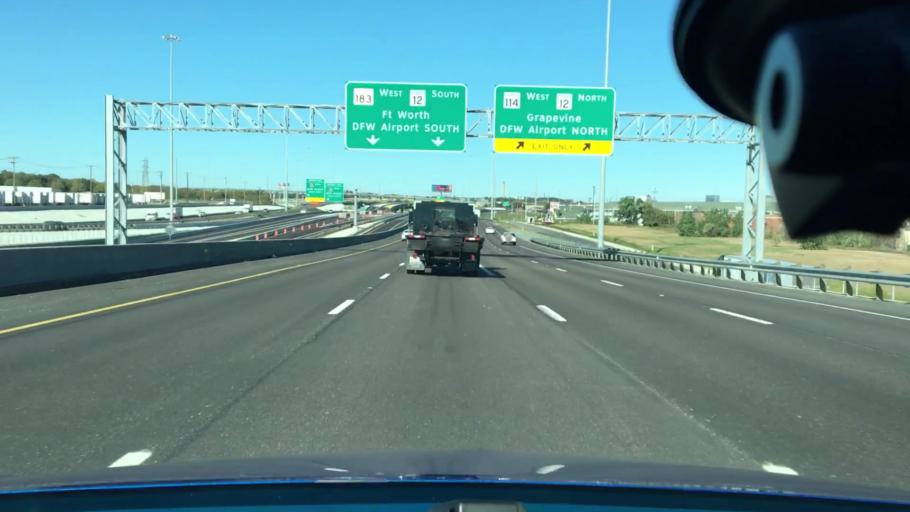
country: US
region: Texas
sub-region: Dallas County
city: Irving
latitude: 32.8341
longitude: -96.8962
